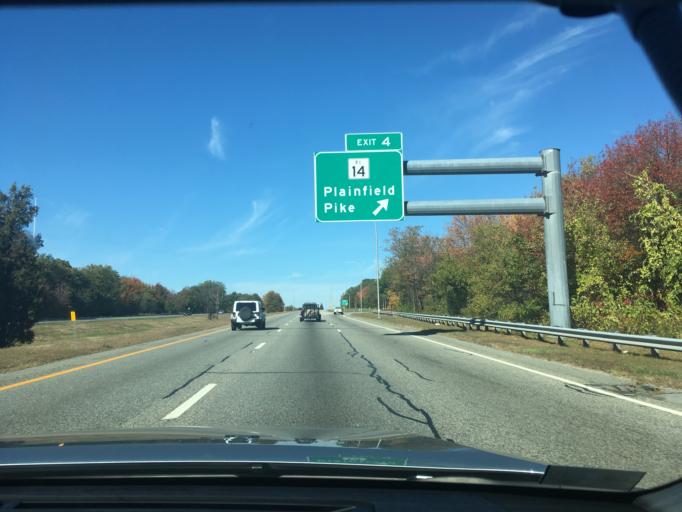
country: US
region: Rhode Island
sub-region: Providence County
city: Johnston
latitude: 41.7844
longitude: -71.5034
